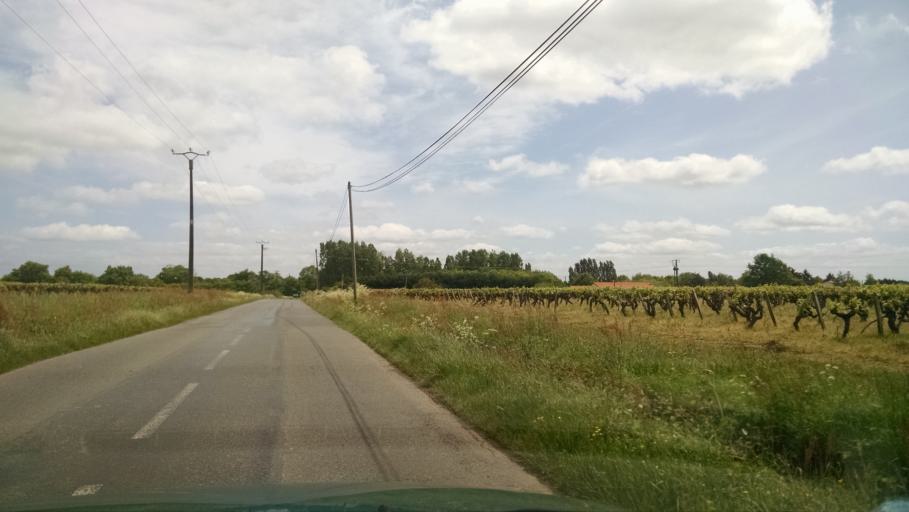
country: FR
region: Pays de la Loire
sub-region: Departement de la Loire-Atlantique
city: Gorges
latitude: 47.0897
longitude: -1.3089
